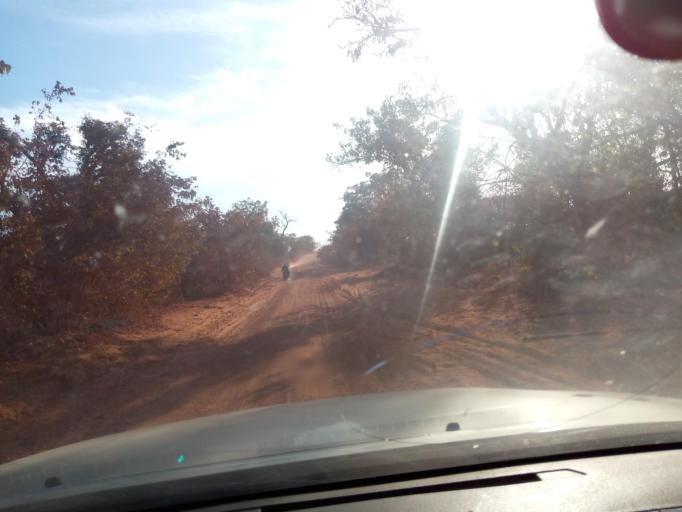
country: ML
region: Sikasso
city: Sikasso
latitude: 11.4270
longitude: -5.5592
